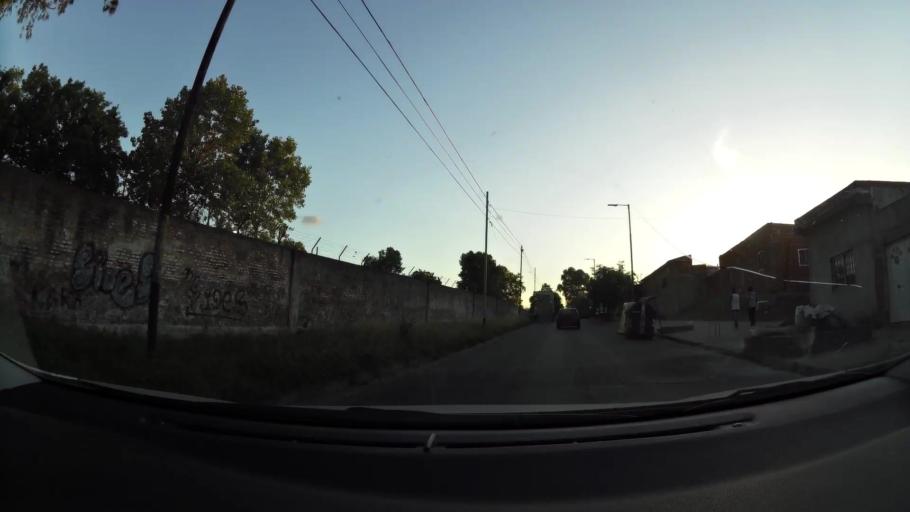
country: AR
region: Buenos Aires F.D.
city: Villa Lugano
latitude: -34.6672
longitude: -58.4687
